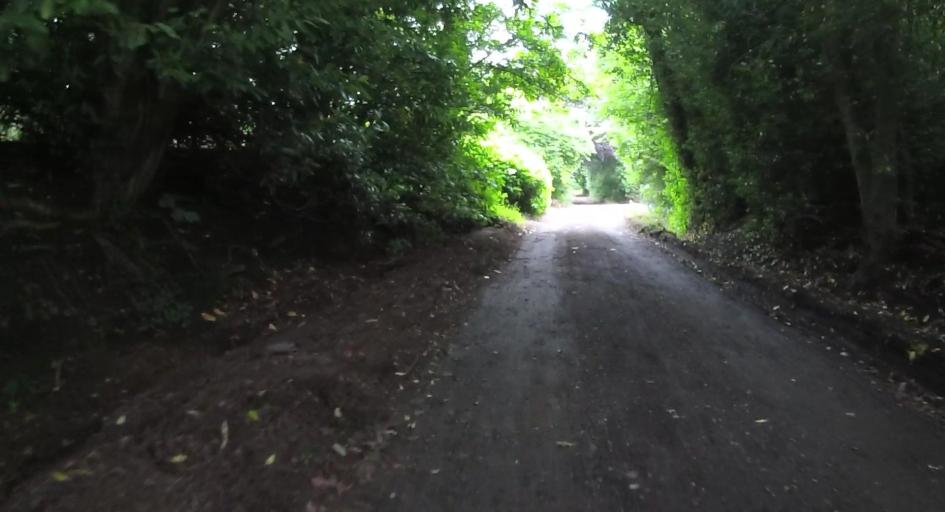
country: GB
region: England
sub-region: Wokingham
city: Finchampstead
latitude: 51.3667
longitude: -0.8499
